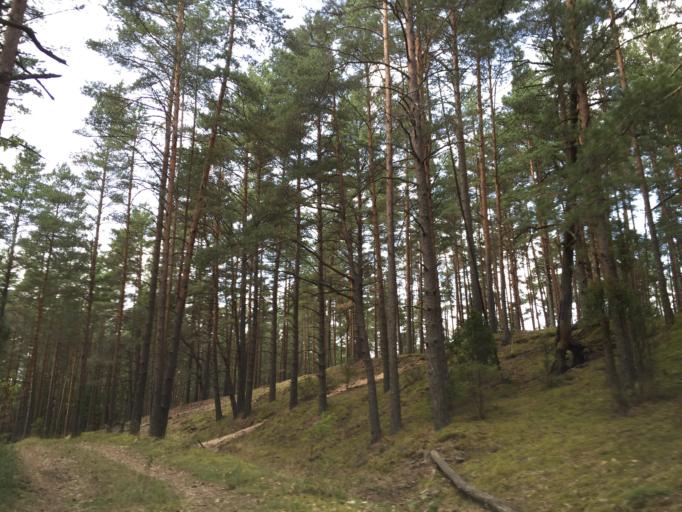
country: LV
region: Jurmala
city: Jurmala
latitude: 56.8713
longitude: 23.7076
